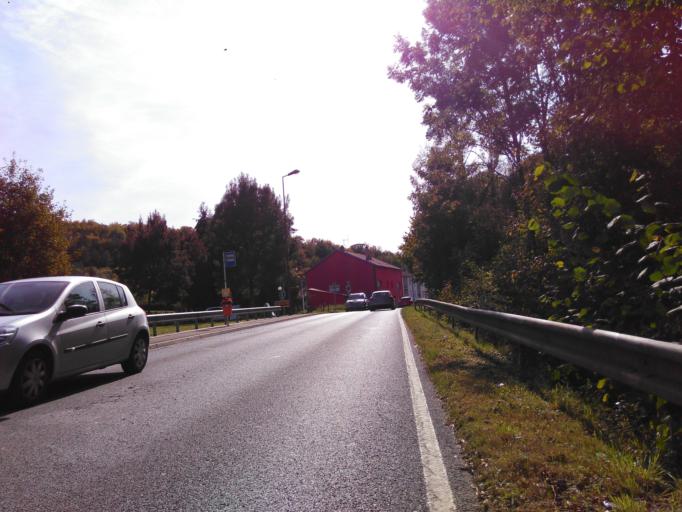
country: LU
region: Luxembourg
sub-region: Canton d'Esch-sur-Alzette
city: Rumelange
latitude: 49.4513
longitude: 6.0259
